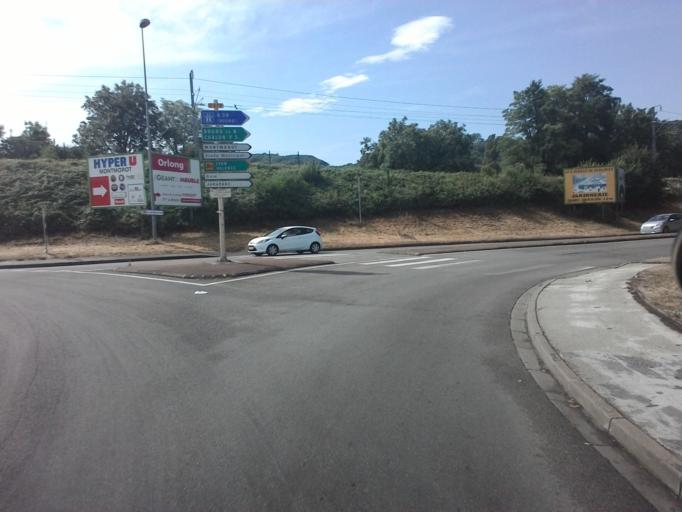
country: FR
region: Franche-Comte
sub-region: Departement du Jura
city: Perrigny
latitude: 46.6704
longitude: 5.5716
